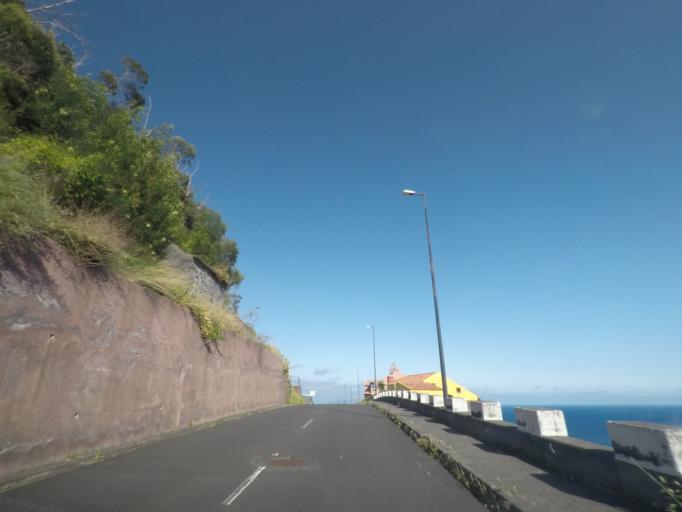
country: PT
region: Madeira
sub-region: Santa Cruz
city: Santa Cruz
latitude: 32.6911
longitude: -16.7943
